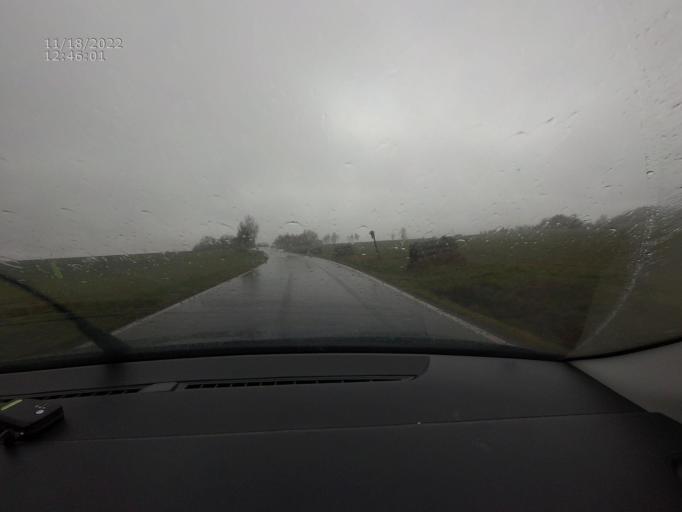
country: CZ
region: Plzensky
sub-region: Okres Klatovy
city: Kolinec
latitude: 49.3501
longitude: 13.4381
